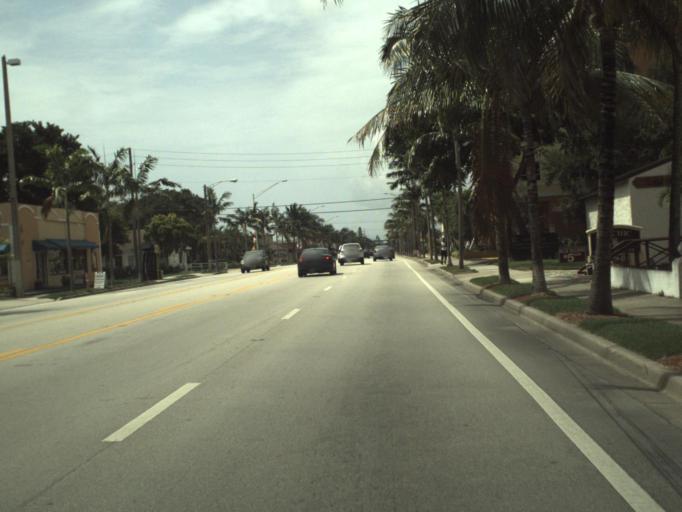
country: US
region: Florida
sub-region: Broward County
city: Dania Beach
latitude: 26.0568
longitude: -80.1439
